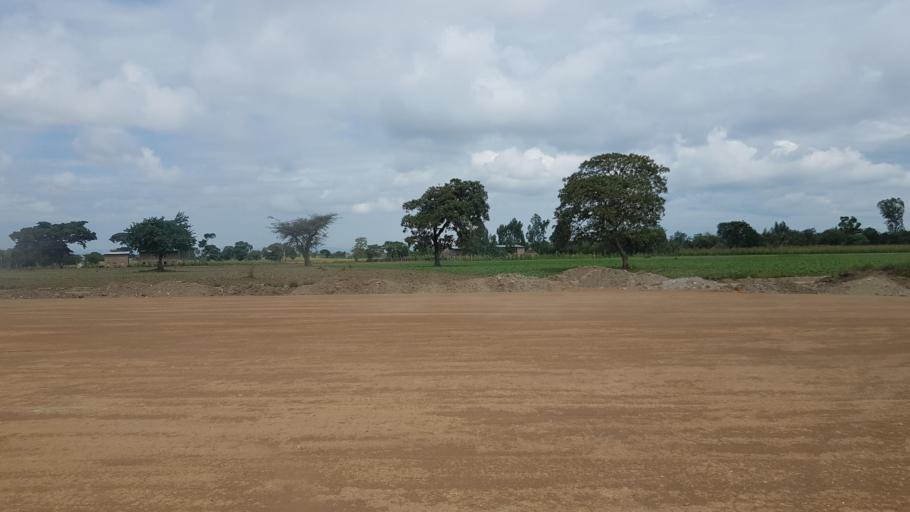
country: ET
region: Oromiya
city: Shashemene
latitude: 7.2576
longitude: 38.5947
